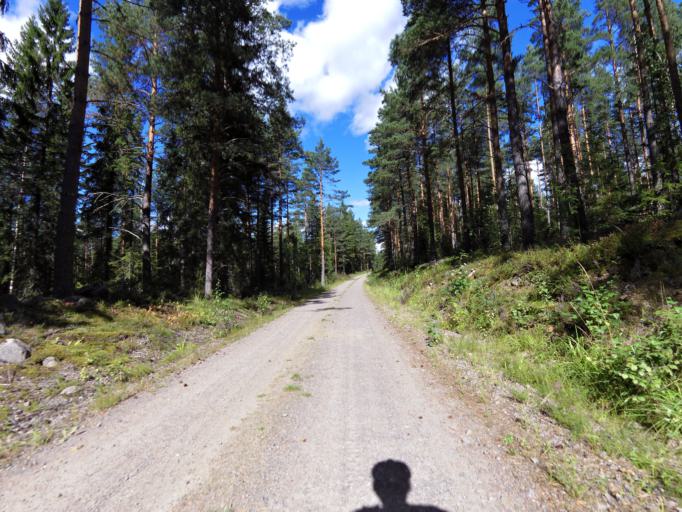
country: SE
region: Gaevleborg
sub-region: Ockelbo Kommun
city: Ockelbo
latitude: 60.8005
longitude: 16.8106
